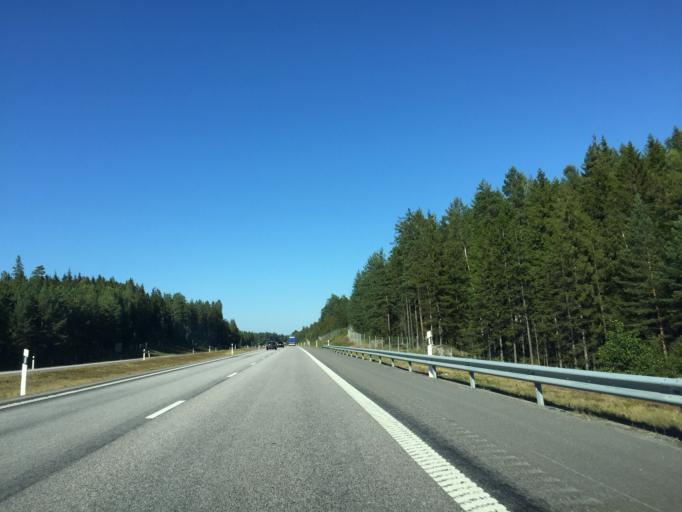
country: SE
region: OErebro
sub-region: Lindesbergs Kommun
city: Fellingsbro
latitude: 59.3547
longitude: 15.5631
